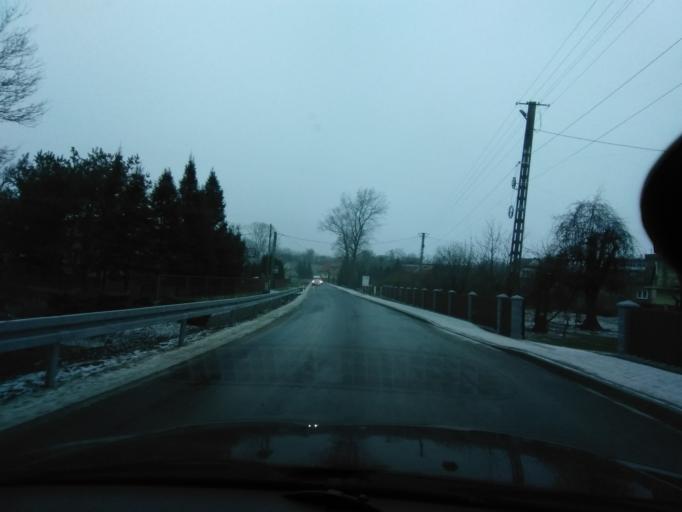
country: PL
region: Subcarpathian Voivodeship
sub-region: Powiat przeworski
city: Gac
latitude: 50.0231
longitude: 22.3936
